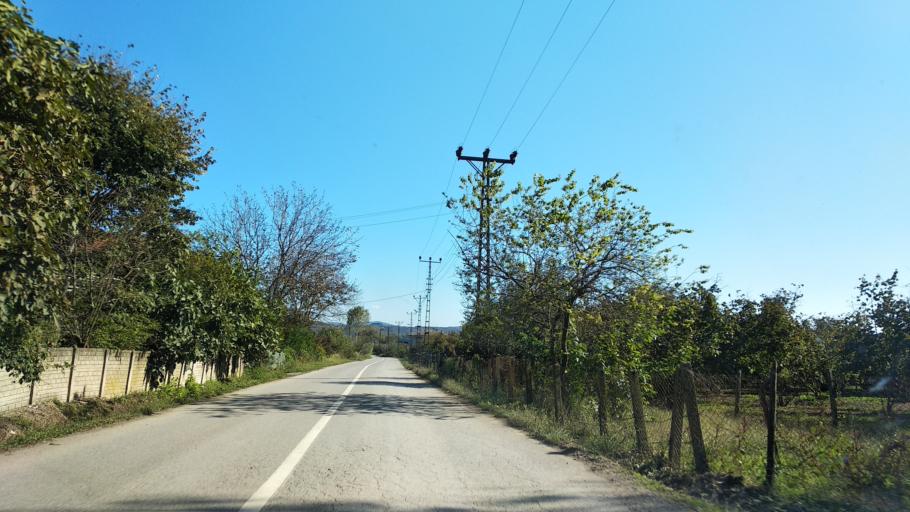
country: TR
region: Sakarya
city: Ortakoy
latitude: 41.0267
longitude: 30.5970
